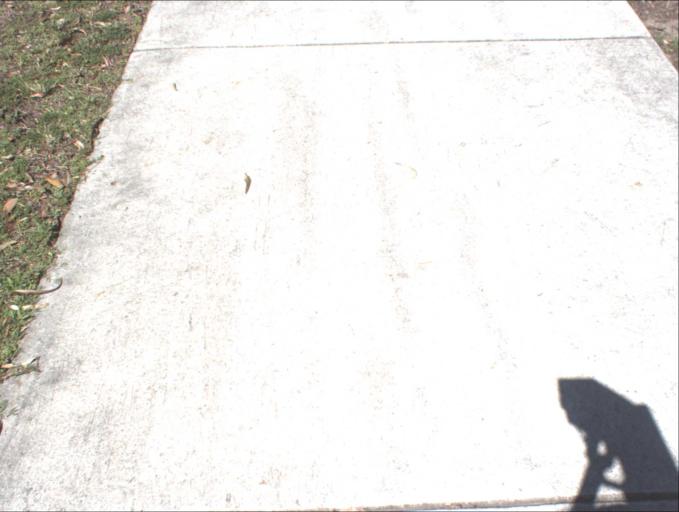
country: AU
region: Queensland
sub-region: Logan
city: Waterford West
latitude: -27.7128
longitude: 153.1597
